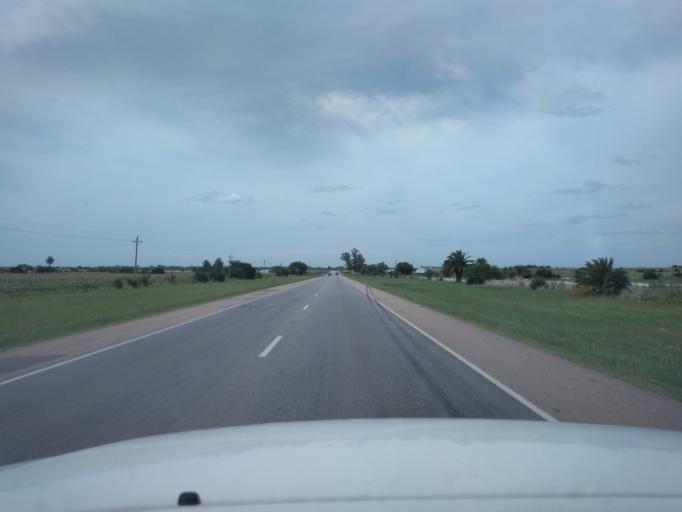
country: UY
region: Canelones
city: Canelones
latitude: -34.3948
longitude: -56.2557
